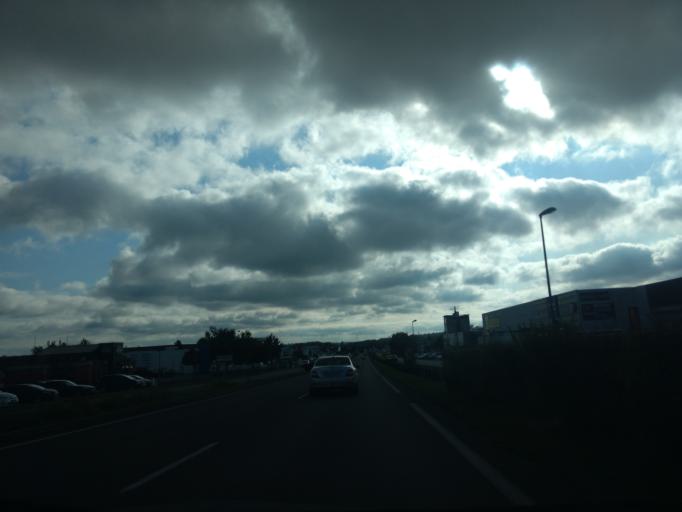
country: FR
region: Poitou-Charentes
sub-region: Departement de la Vienne
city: Chasseneuil-du-Poitou
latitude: 46.6515
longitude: 0.3643
